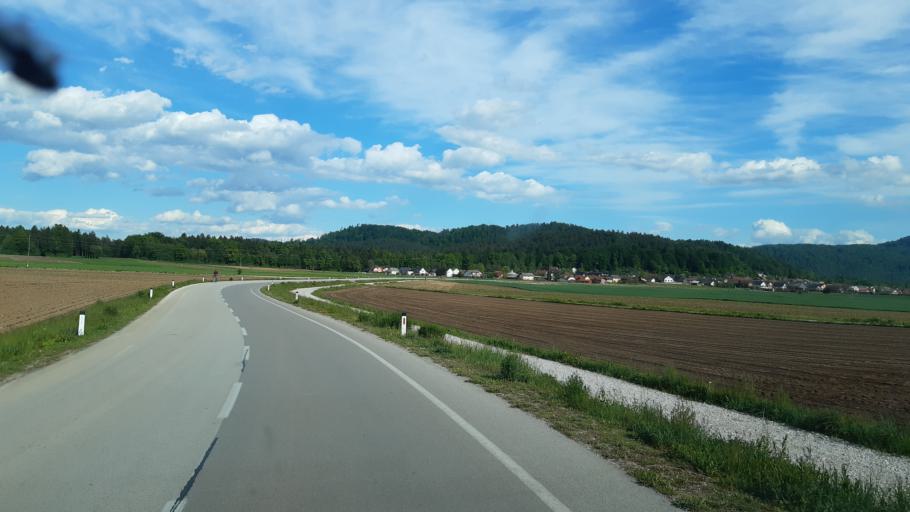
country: SI
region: Vodice
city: Vodice
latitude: 46.1828
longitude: 14.4980
